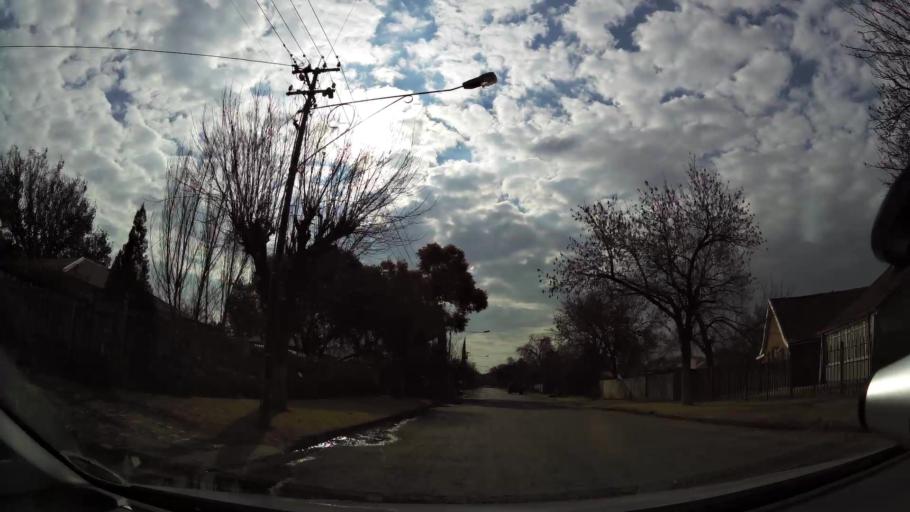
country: ZA
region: Orange Free State
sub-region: Mangaung Metropolitan Municipality
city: Bloemfontein
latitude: -29.0892
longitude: 26.2517
